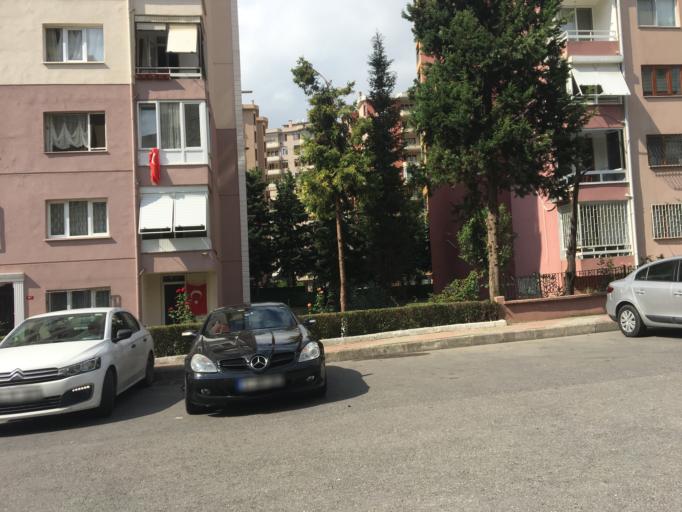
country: TR
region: Istanbul
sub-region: Atasehir
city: Atasehir
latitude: 40.9653
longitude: 29.0972
